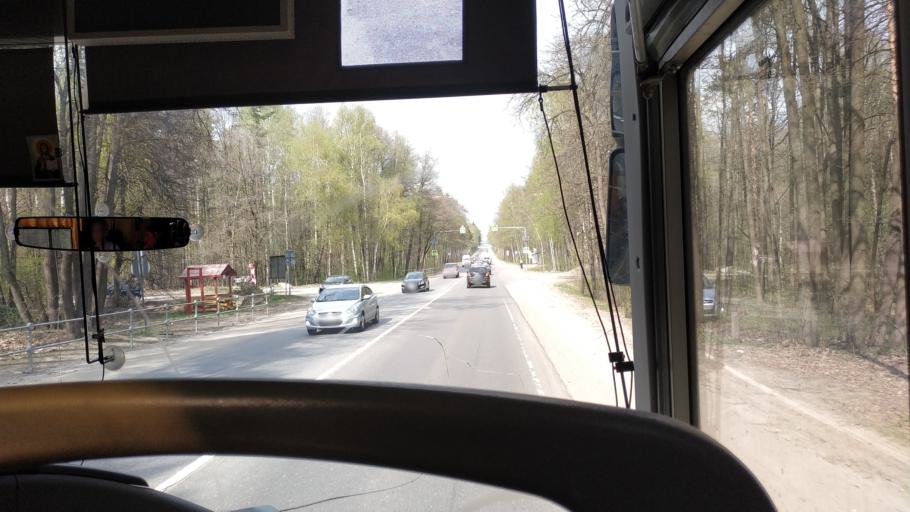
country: RU
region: Moskovskaya
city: Lytkarino
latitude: 55.6035
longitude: 37.9160
